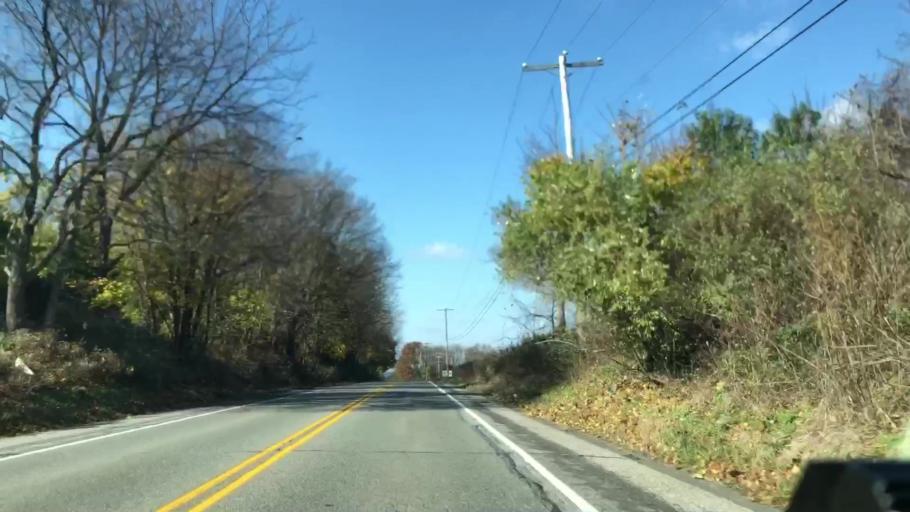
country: US
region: Pennsylvania
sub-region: Chester County
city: Kenilworth
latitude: 40.2188
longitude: -75.6091
